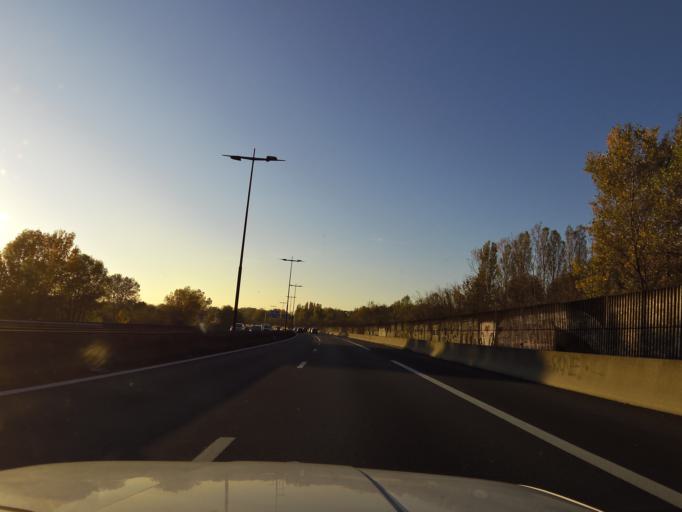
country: FR
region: Rhone-Alpes
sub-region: Departement du Rhone
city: Vaulx-en-Velin
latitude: 45.7965
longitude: 4.9438
